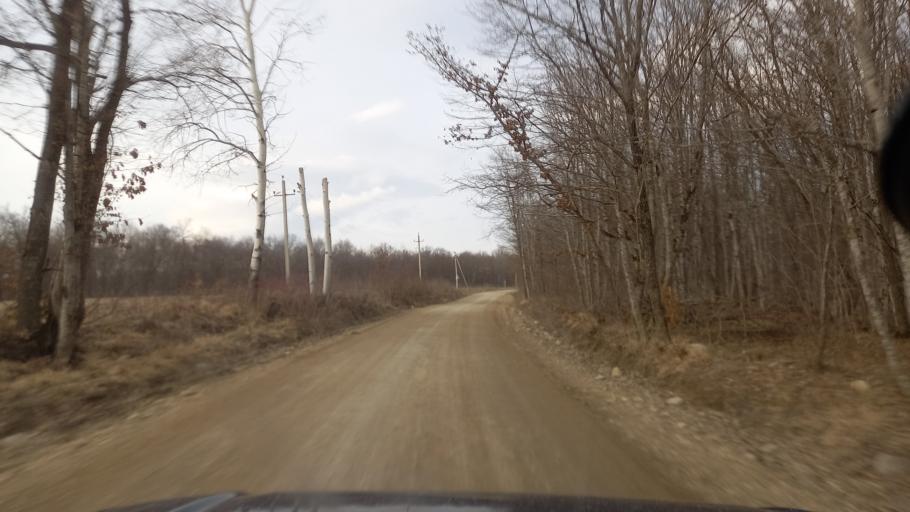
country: RU
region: Adygeya
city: Kamennomostskiy
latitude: 44.1419
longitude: 40.2578
